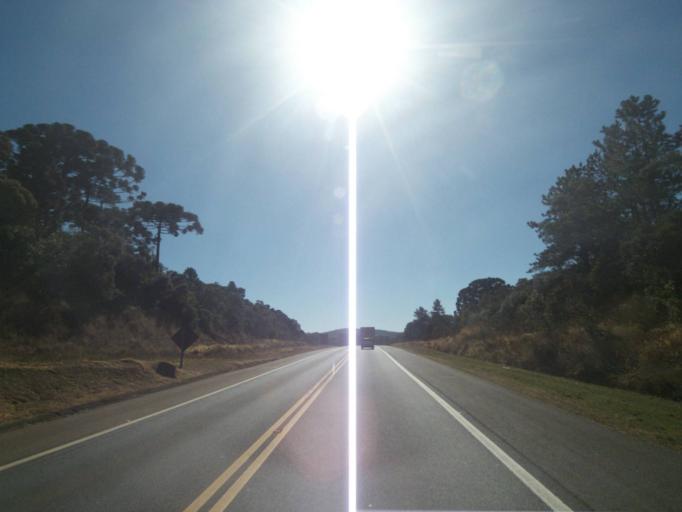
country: BR
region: Parana
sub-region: Tibagi
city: Tibagi
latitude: -24.7278
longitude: -50.5383
